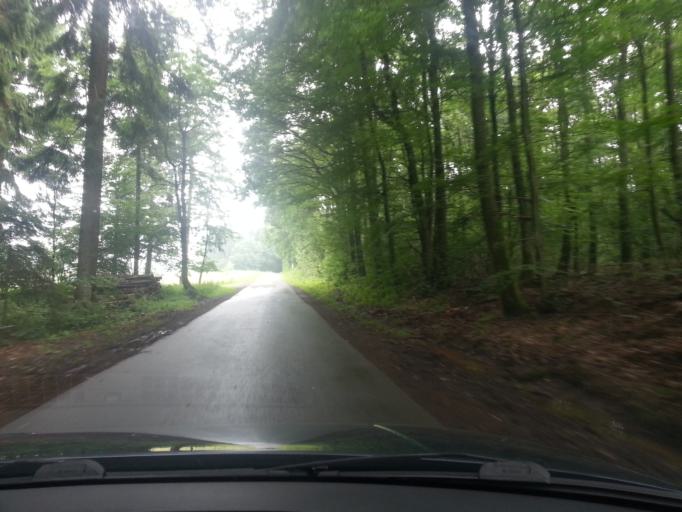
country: DE
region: Saarland
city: Mainzweiler
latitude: 49.4390
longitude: 7.0944
